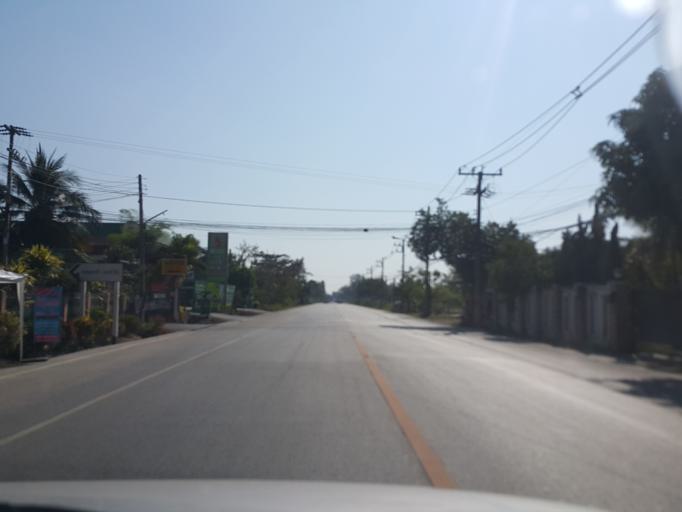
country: TH
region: Chiang Mai
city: San Kamphaeng
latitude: 18.8035
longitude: 99.1119
